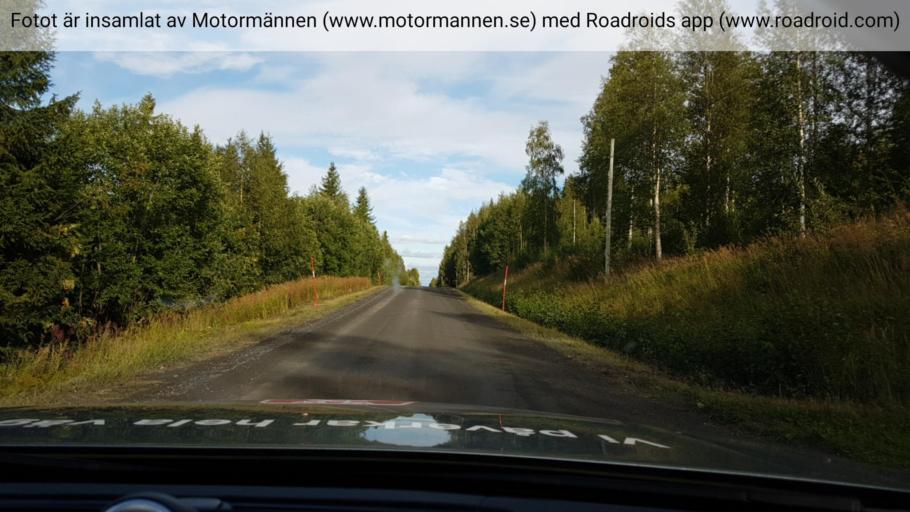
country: SE
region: Jaemtland
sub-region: Stroemsunds Kommun
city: Stroemsund
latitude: 64.1429
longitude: 15.7113
